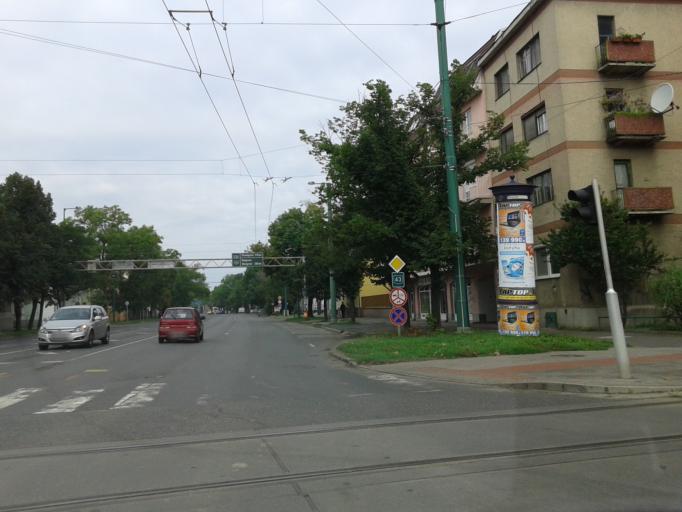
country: HU
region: Csongrad
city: Szeged
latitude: 46.2614
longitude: 20.1576
